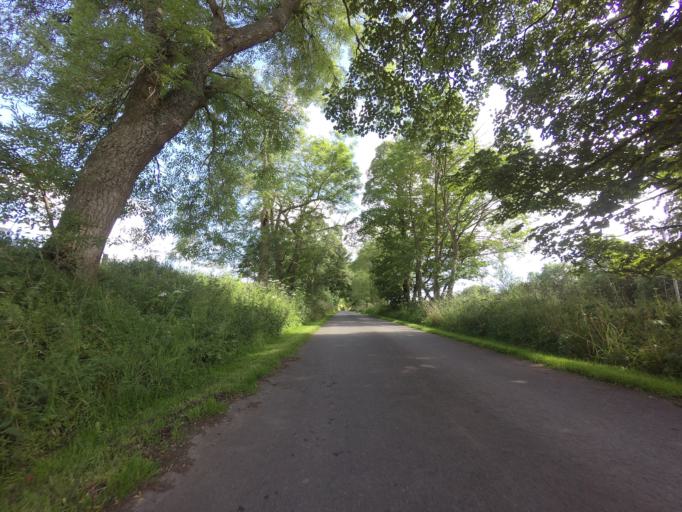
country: GB
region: Scotland
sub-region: Aberdeenshire
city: Turriff
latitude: 57.5924
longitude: -2.5071
